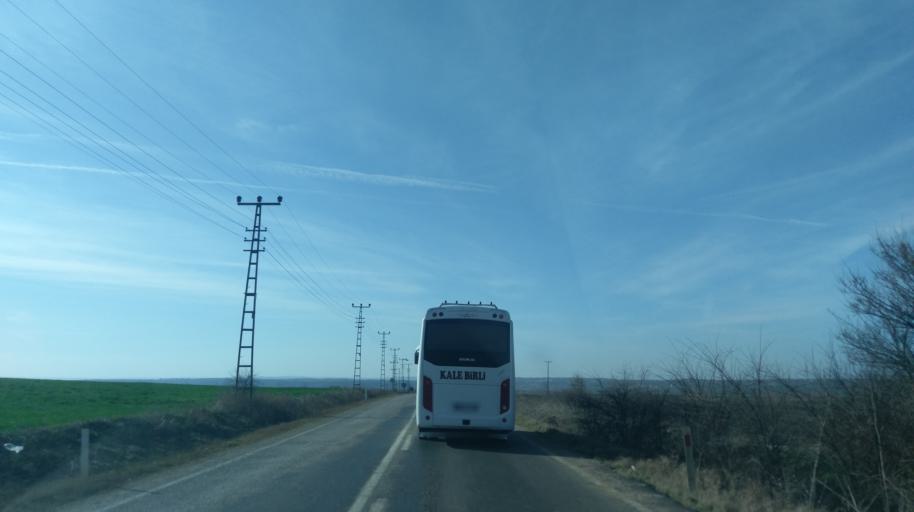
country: TR
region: Edirne
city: Copkoy
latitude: 41.3042
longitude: 26.8162
